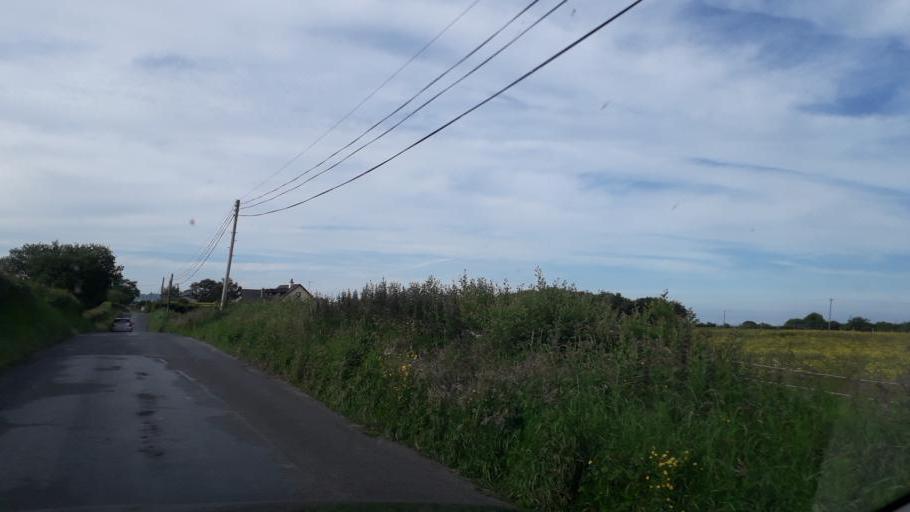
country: IE
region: Leinster
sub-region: Loch Garman
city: Courtown
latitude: 52.5890
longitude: -6.2304
